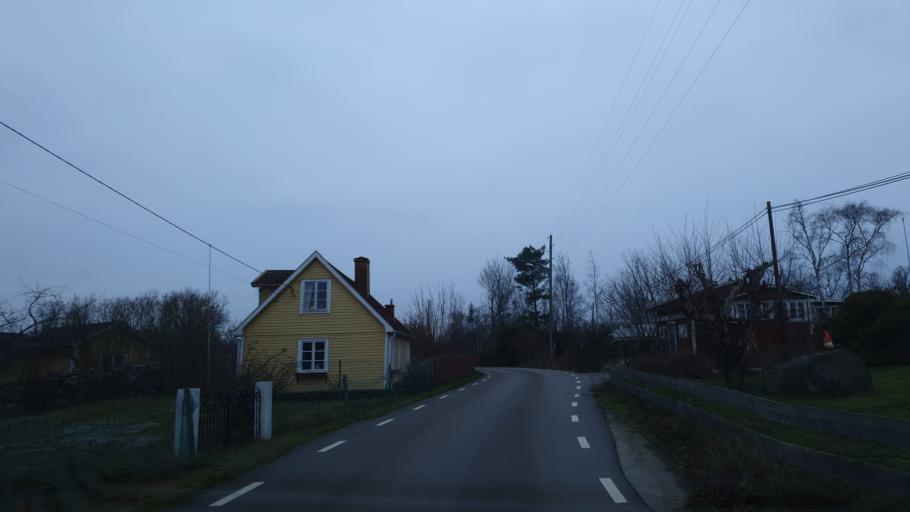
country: SE
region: Blekinge
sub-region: Karlskrona Kommun
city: Karlskrona
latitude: 56.1244
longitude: 15.6255
